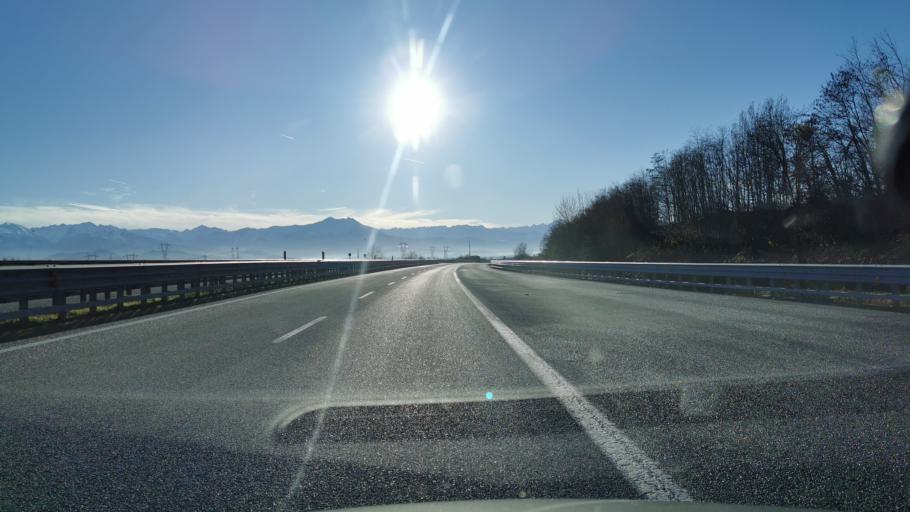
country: IT
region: Piedmont
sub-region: Provincia di Cuneo
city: Magliano Alpi
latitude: 44.4751
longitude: 7.7899
